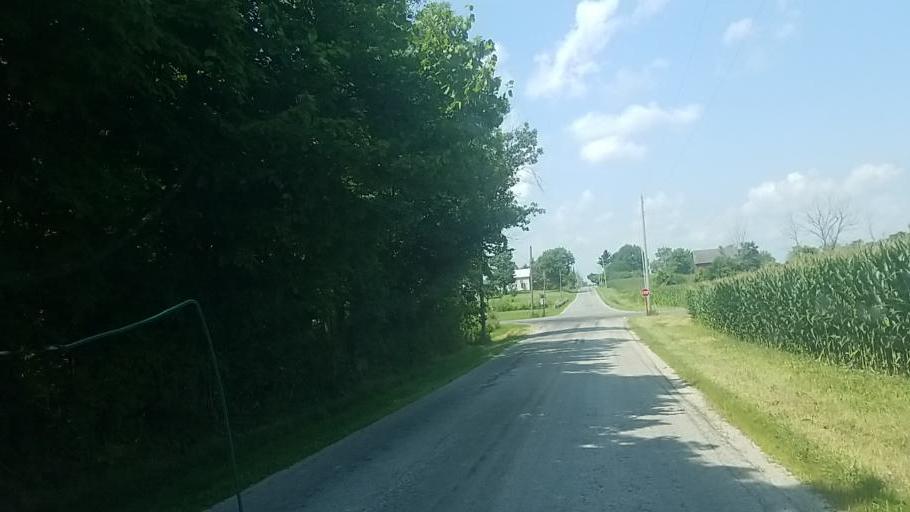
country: US
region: Ohio
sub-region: Crawford County
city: Crestline
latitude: 40.7988
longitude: -82.6969
